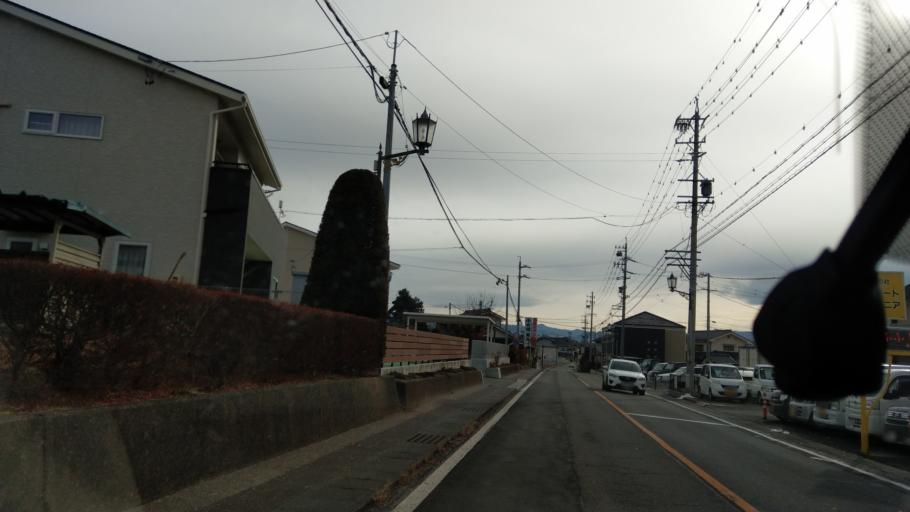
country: JP
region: Nagano
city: Komoro
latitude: 36.2851
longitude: 138.4634
